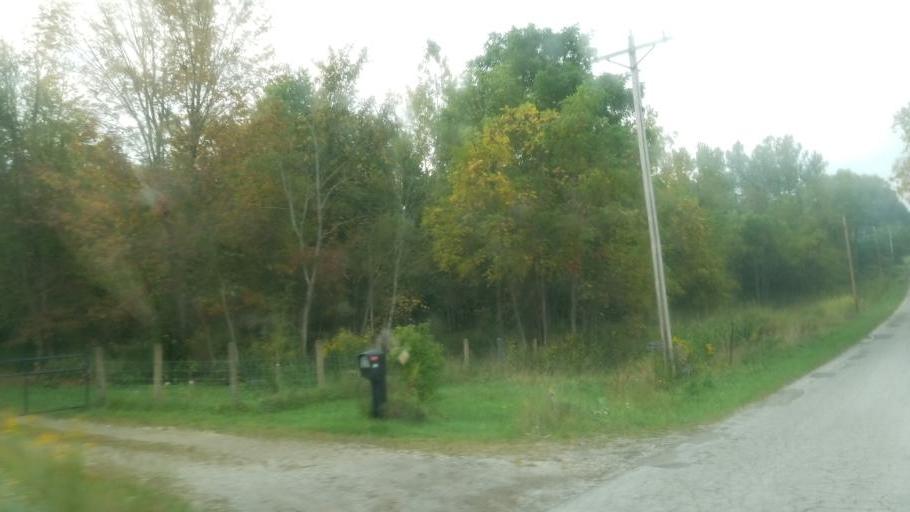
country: US
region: Ohio
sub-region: Knox County
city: Fredericktown
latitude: 40.4218
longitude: -82.6504
